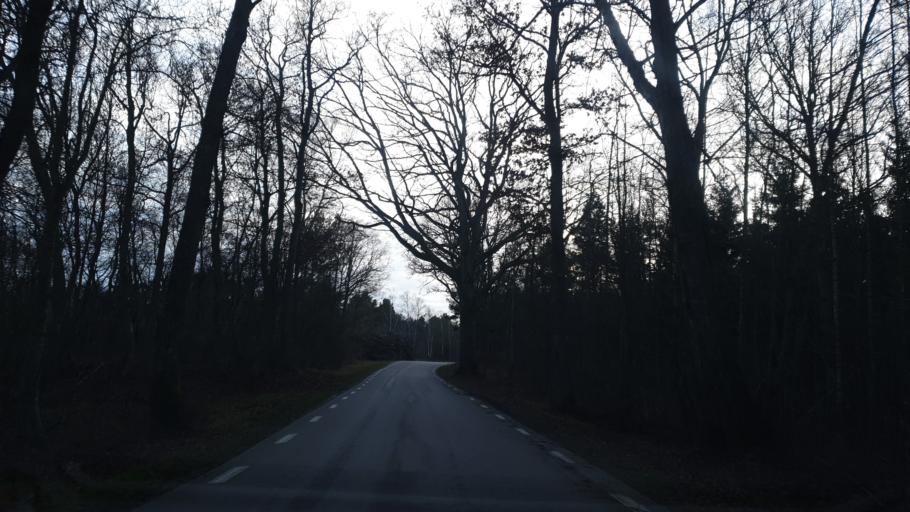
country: SE
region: Blekinge
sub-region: Karlskrona Kommun
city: Jaemjoe
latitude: 56.1395
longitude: 15.8930
